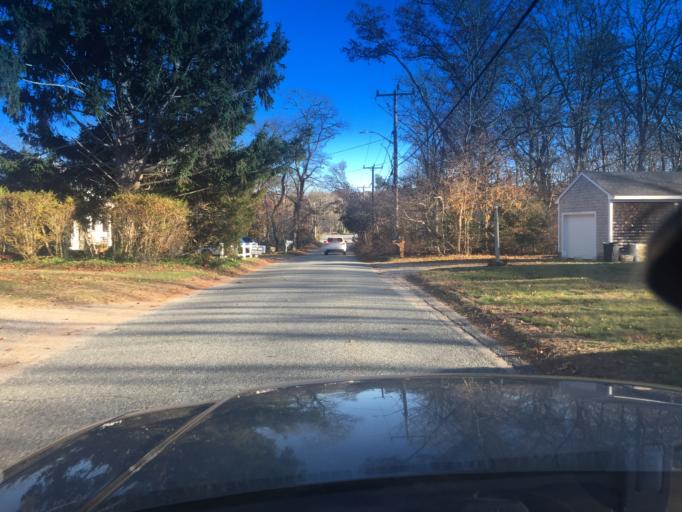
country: US
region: Massachusetts
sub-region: Barnstable County
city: North Falmouth
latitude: 41.6398
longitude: -70.6184
